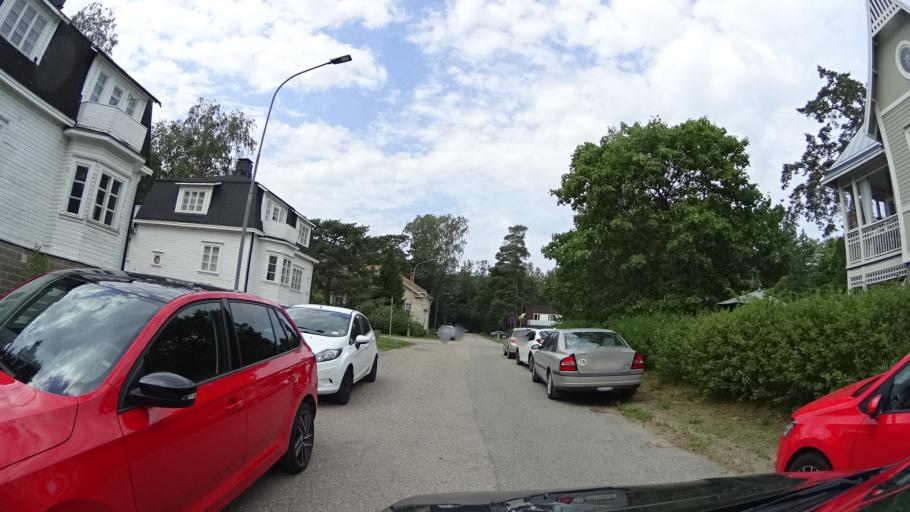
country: FI
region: Uusimaa
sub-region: Raaseporin
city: Hanko
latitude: 59.8263
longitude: 22.9802
